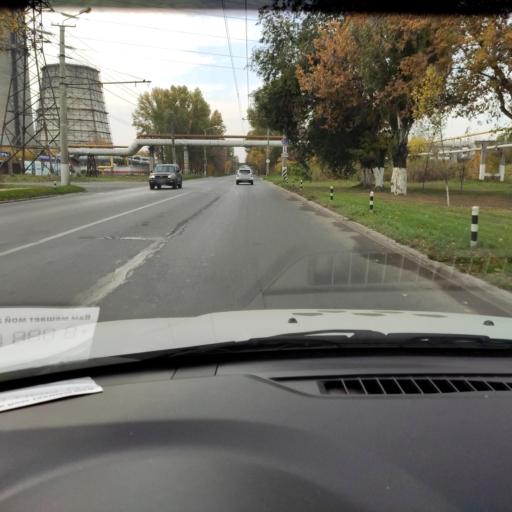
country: RU
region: Samara
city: Tol'yatti
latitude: 53.5517
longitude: 49.4492
